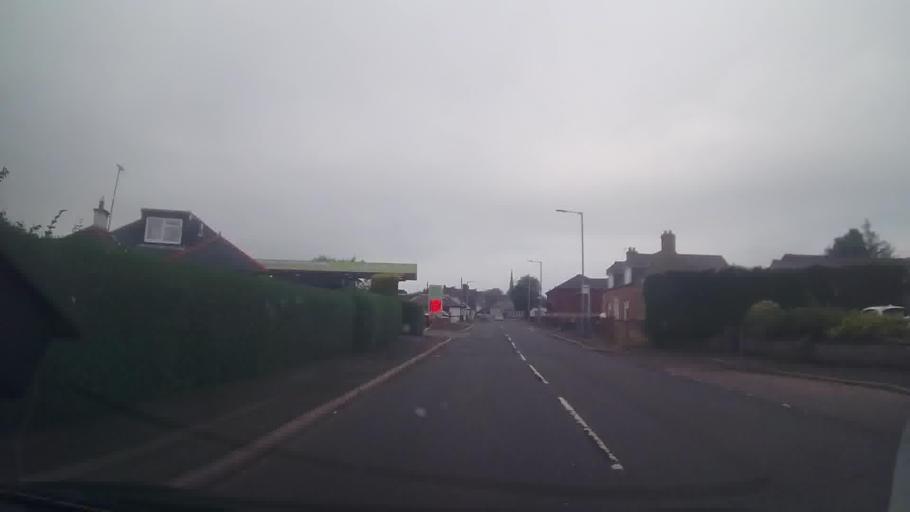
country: GB
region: Scotland
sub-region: Dumfries and Galloway
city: Lockerbie
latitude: 55.1164
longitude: -3.3560
